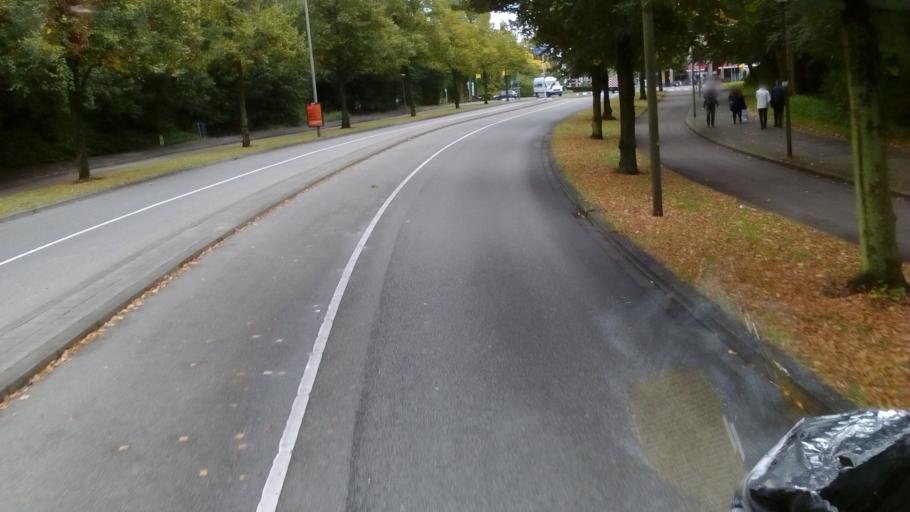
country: NL
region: South Holland
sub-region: Gemeente Schiedam
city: Schiedam
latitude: 51.9181
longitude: 4.3904
